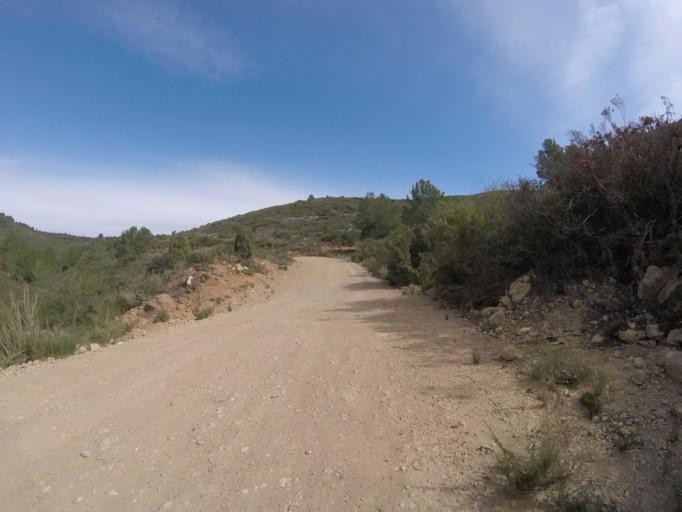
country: ES
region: Valencia
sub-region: Provincia de Castello
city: Torreblanca
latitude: 40.2019
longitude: 0.1518
